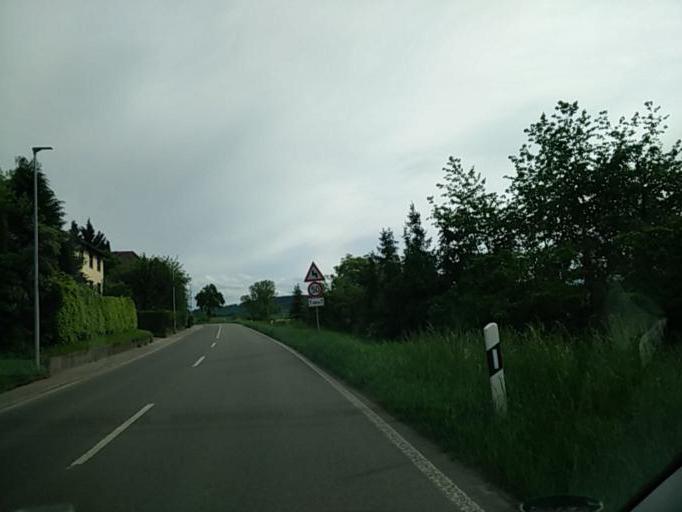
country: DE
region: Baden-Wuerttemberg
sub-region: Regierungsbezirk Stuttgart
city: Hildrizhausen
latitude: 48.5485
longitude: 8.9657
